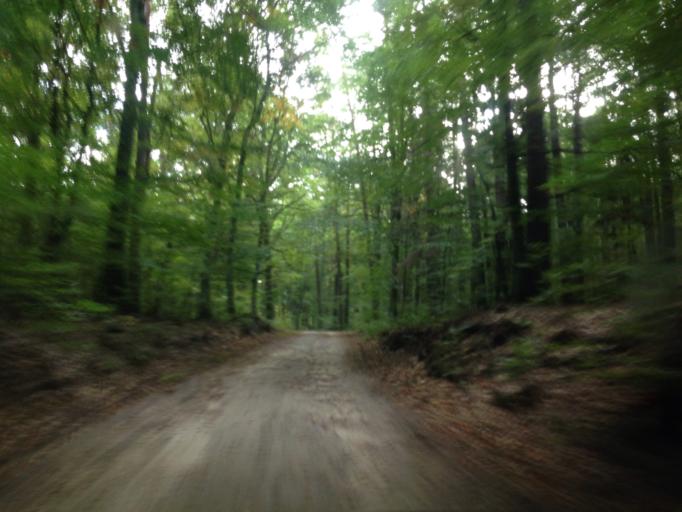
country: PL
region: Warmian-Masurian Voivodeship
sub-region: Powiat ilawski
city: Susz
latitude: 53.7674
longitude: 19.3199
